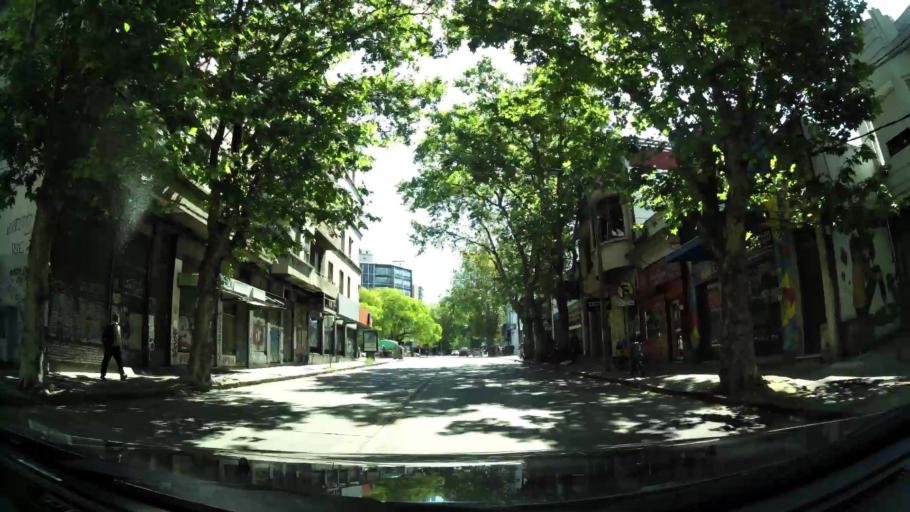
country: UY
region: Montevideo
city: Montevideo
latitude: -34.9032
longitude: -56.1549
